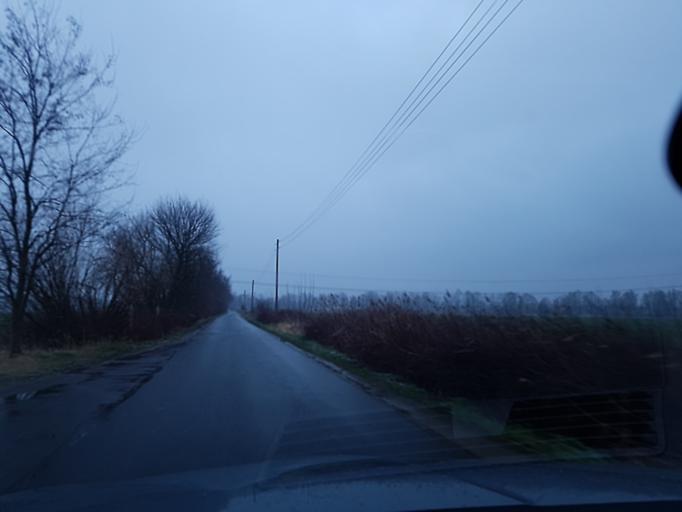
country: DE
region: Brandenburg
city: Groden
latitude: 51.4336
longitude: 13.5556
